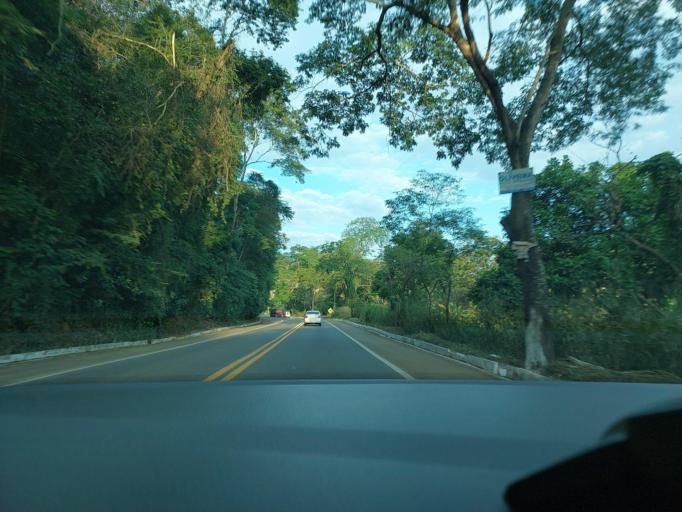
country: BR
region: Minas Gerais
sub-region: Muriae
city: Muriae
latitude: -21.1263
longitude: -42.2788
